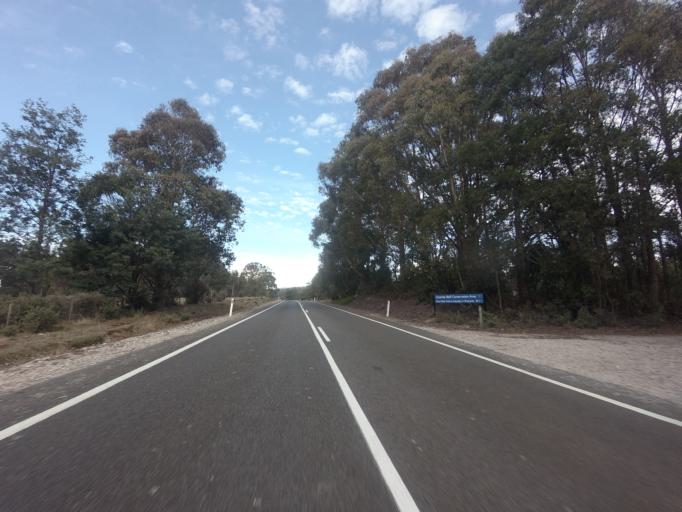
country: AU
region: Tasmania
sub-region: Meander Valley
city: Deloraine
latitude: -41.6602
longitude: 146.7227
